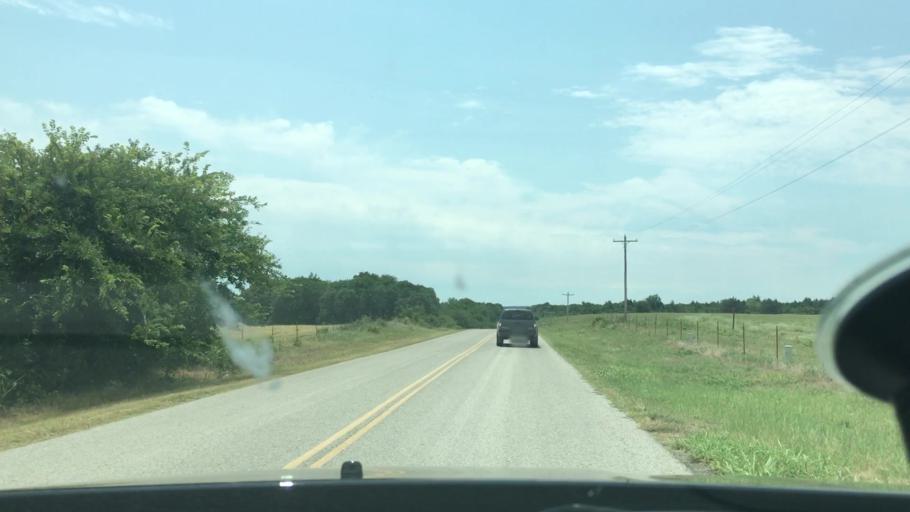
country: US
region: Oklahoma
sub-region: Love County
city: Marietta
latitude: 33.9089
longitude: -97.3522
